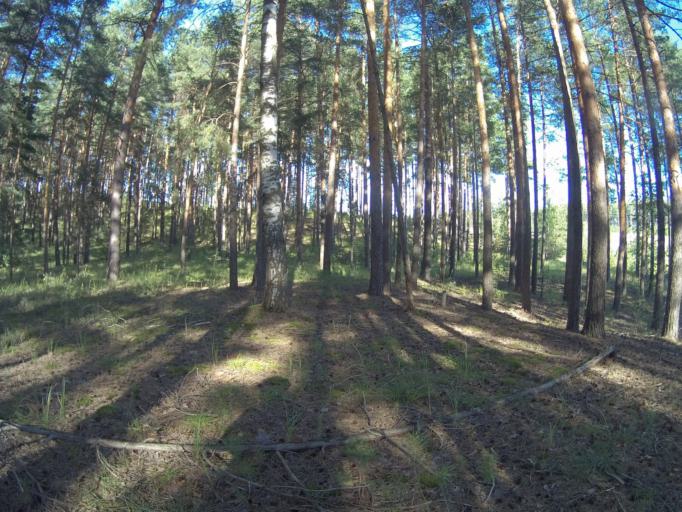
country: RU
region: Vladimir
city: Kommunar
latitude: 56.0565
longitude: 40.4363
